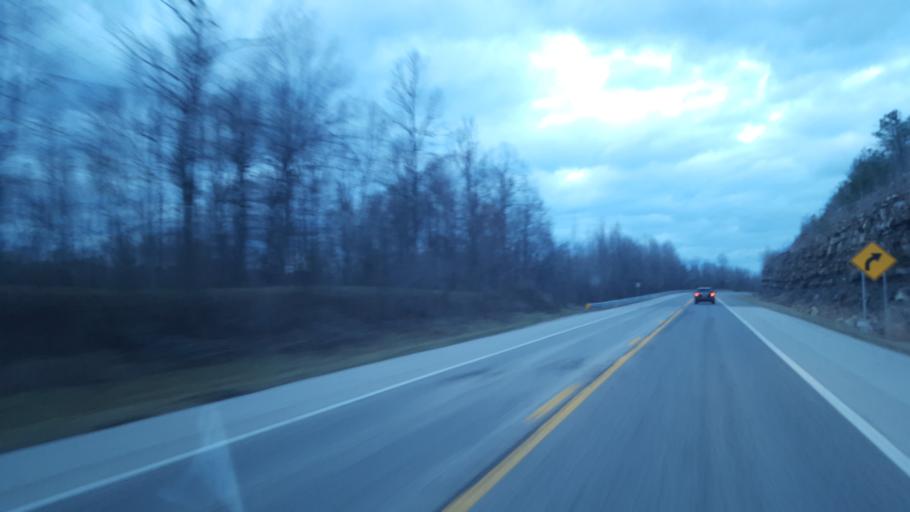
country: US
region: Kentucky
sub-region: Lewis County
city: Vanceburg
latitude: 38.6010
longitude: -83.1697
